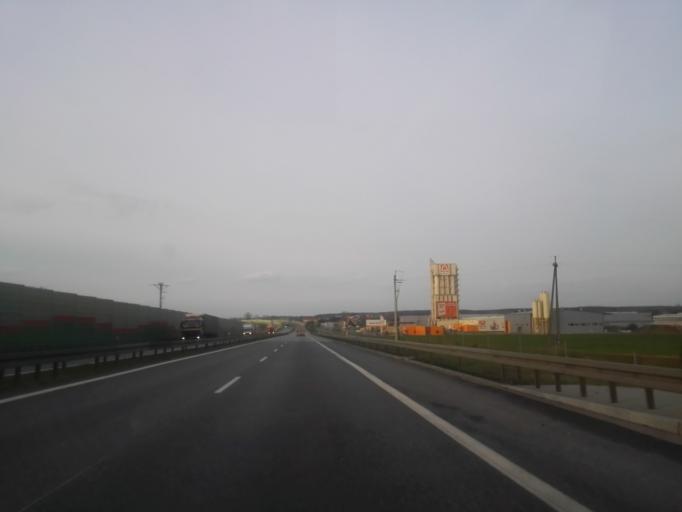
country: PL
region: Lodz Voivodeship
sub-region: Powiat rawski
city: Rawa Mazowiecka
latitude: 51.7600
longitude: 20.2627
